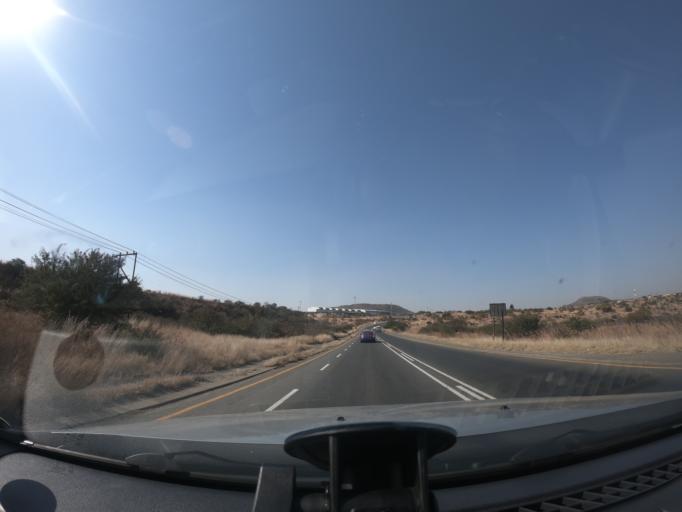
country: ZA
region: KwaZulu-Natal
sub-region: uThukela District Municipality
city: Ladysmith
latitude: -28.5478
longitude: 29.8258
